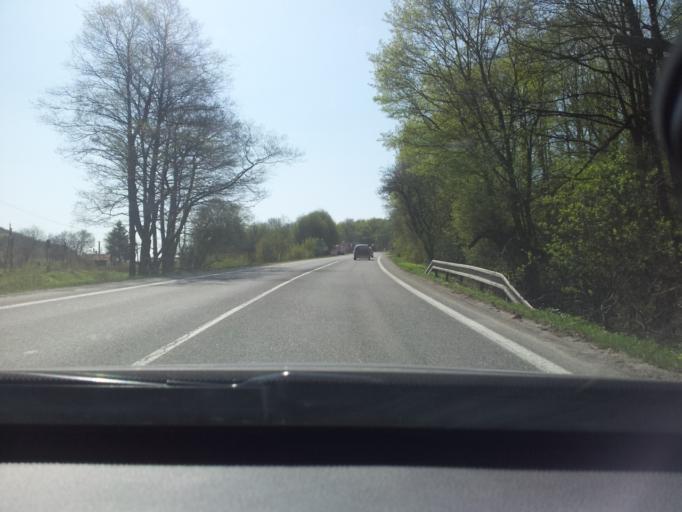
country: SK
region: Trenciansky
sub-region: Okres Trencin
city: Trencin
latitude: 48.8147
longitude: 18.0856
